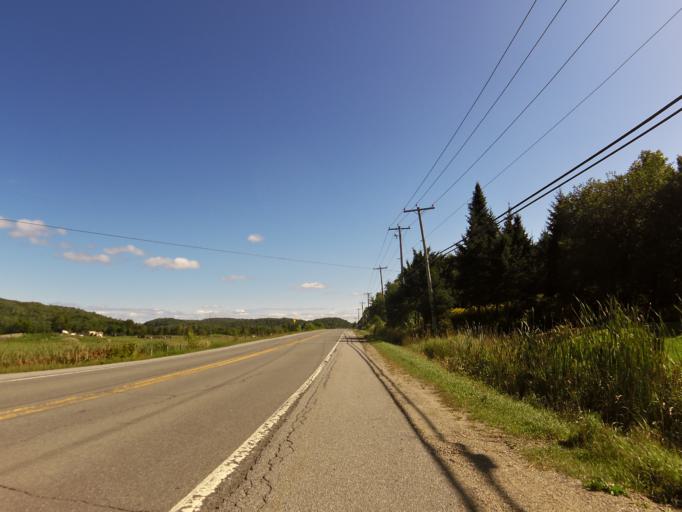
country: CA
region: Quebec
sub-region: Outaouais
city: Val-des-Monts
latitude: 45.6841
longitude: -75.4707
